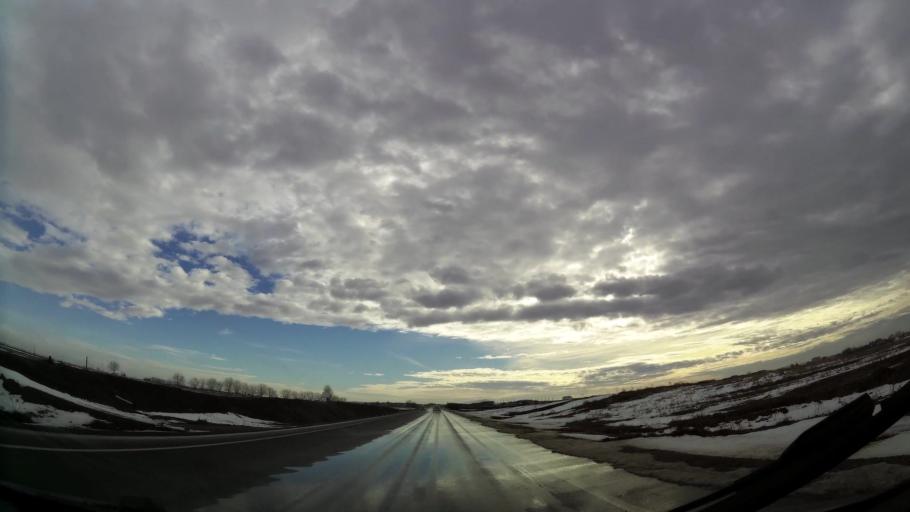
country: RS
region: Central Serbia
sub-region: Belgrade
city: Surcin
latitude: 44.8057
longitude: 20.3078
